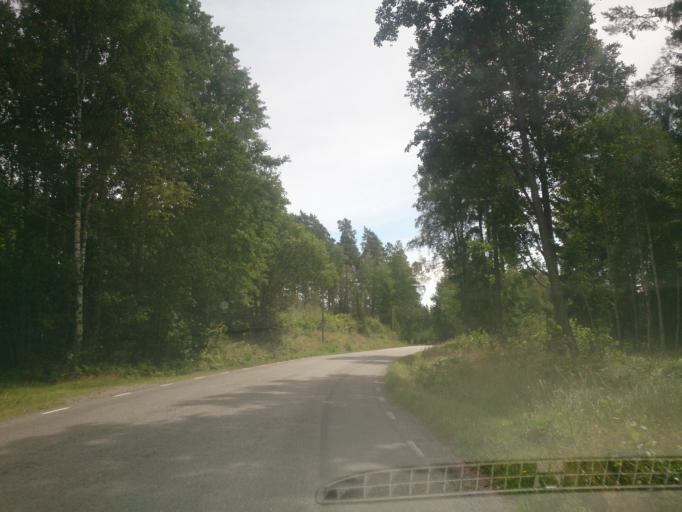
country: SE
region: OEstergoetland
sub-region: Valdemarsviks Kommun
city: Gusum
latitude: 58.3308
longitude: 16.4168
